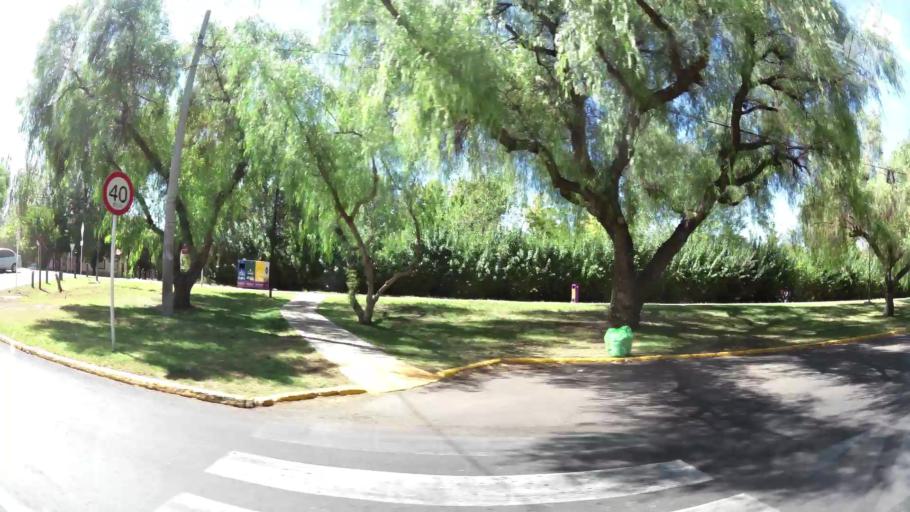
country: AR
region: Mendoza
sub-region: Departamento de Godoy Cruz
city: Godoy Cruz
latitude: -32.9463
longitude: -68.8524
